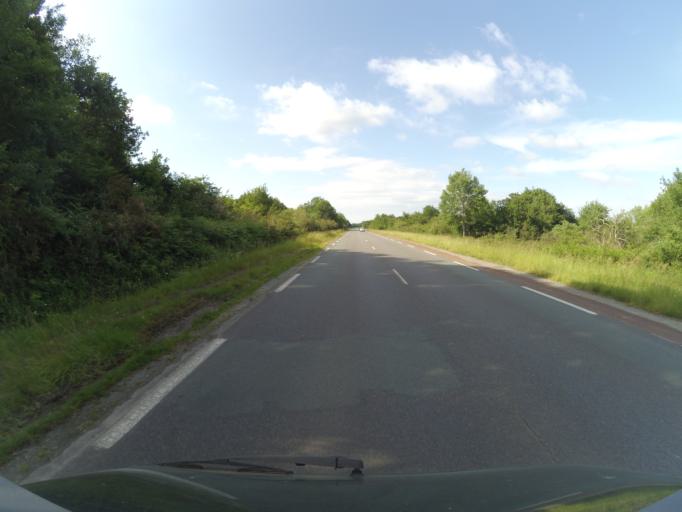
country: FR
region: Poitou-Charentes
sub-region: Departement de la Charente-Maritime
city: Le Gua
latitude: 45.7928
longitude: -0.9361
